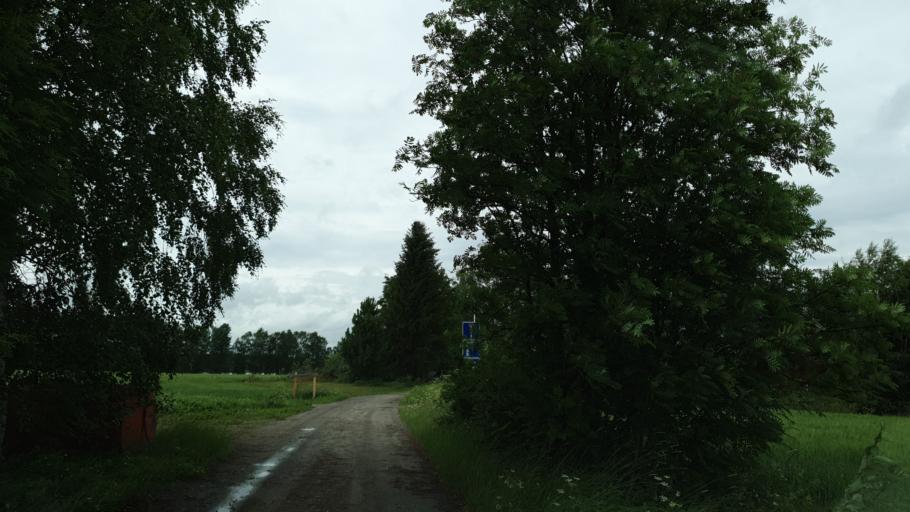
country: FI
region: Kainuu
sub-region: Kehys-Kainuu
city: Kuhmo
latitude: 64.1288
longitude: 29.5707
